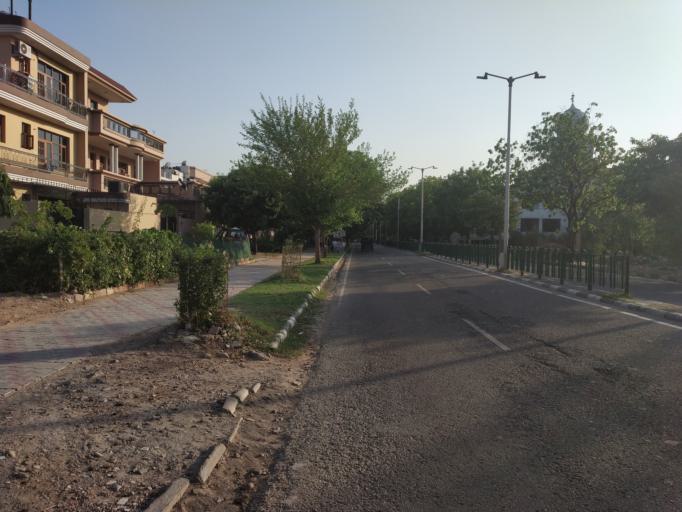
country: IN
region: Punjab
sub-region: Ajitgarh
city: Mohali
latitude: 30.6865
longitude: 76.7477
